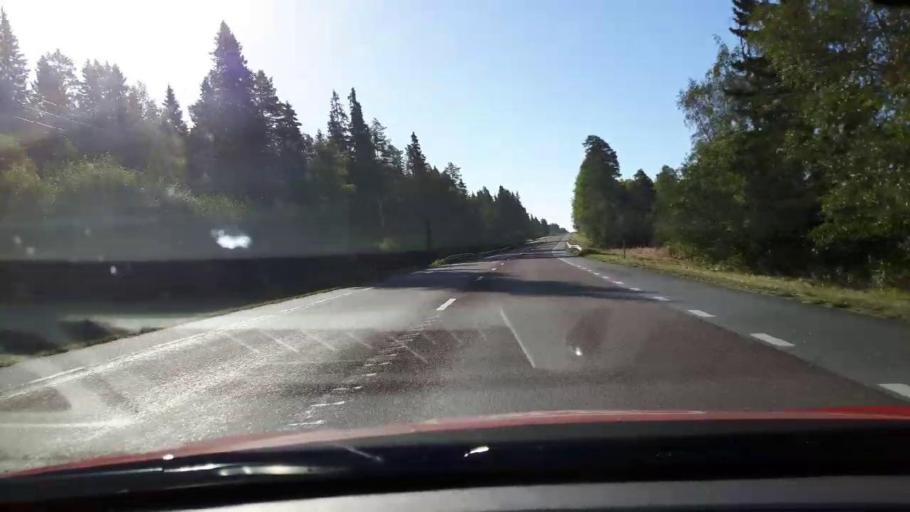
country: SE
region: Jaemtland
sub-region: Braecke Kommun
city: Braecke
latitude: 62.8736
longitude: 15.3021
